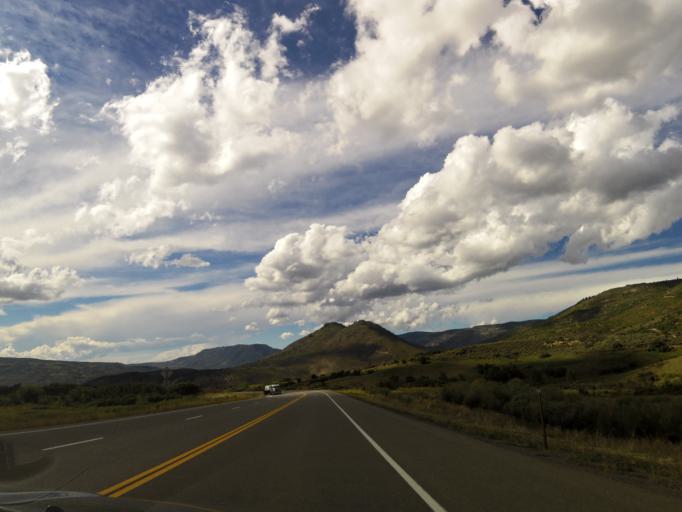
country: US
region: Colorado
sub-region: Hinsdale County
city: Lake City
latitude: 38.3946
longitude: -107.4594
